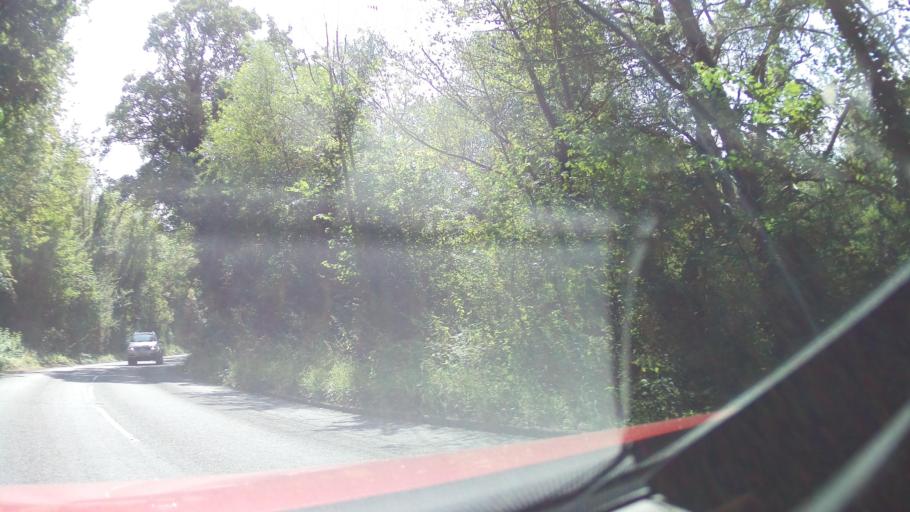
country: GB
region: England
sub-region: Dorset
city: Blandford Forum
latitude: 50.8701
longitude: -2.1713
